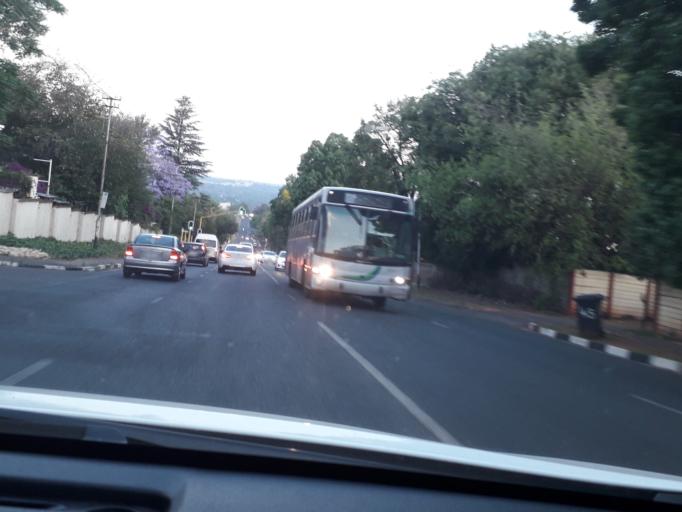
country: ZA
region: Gauteng
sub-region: City of Johannesburg Metropolitan Municipality
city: Johannesburg
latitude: -26.1283
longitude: 27.9981
